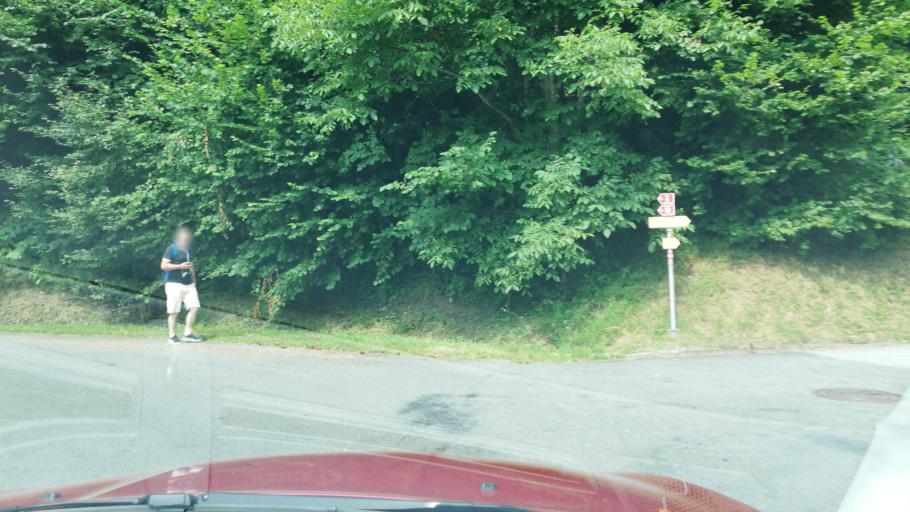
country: AT
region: Upper Austria
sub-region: Politischer Bezirk Rohrbach
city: Kleinzell im Muehlkreis
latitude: 48.4860
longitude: 13.9949
